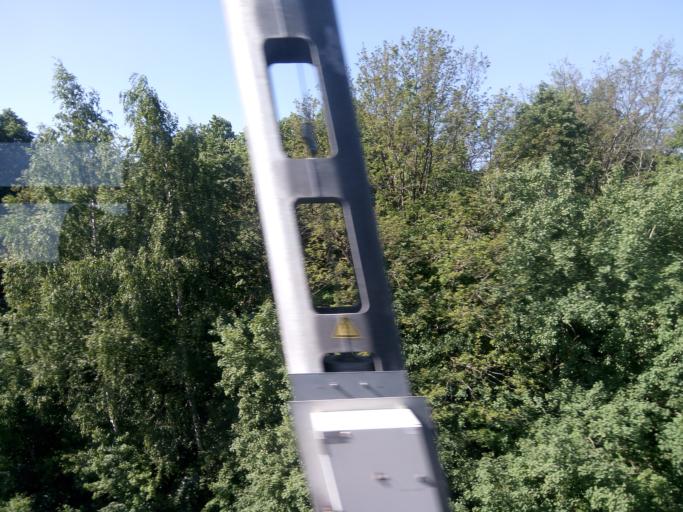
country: RU
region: Tatarstan
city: Stolbishchi
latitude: 55.6128
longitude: 49.2904
